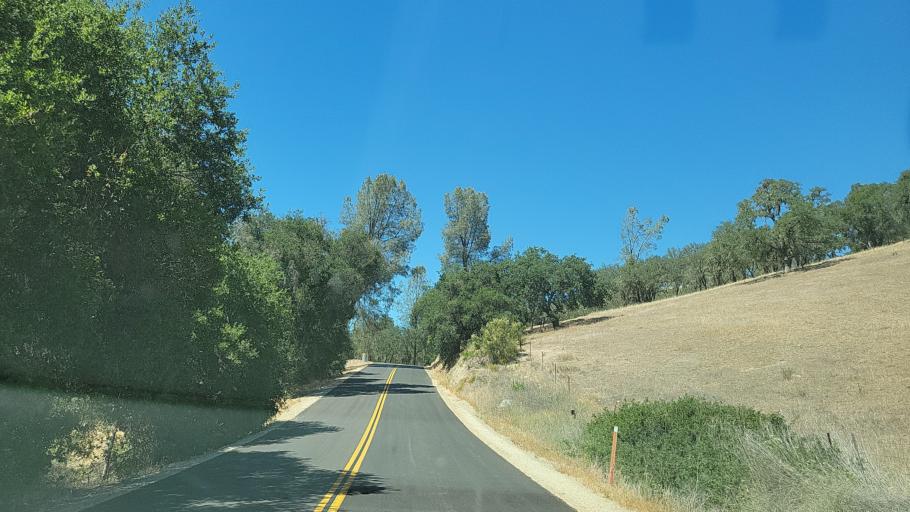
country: US
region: California
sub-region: San Luis Obispo County
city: Atascadero
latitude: 35.4764
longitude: -120.6235
